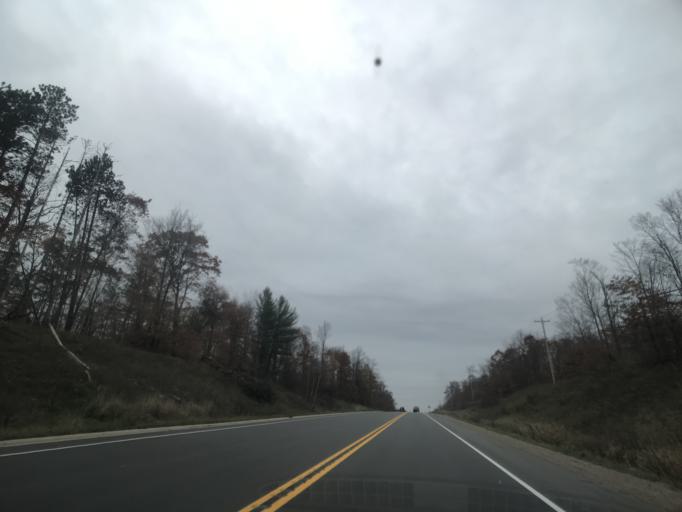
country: US
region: Wisconsin
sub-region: Menominee County
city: Legend Lake
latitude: 45.2458
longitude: -88.5150
